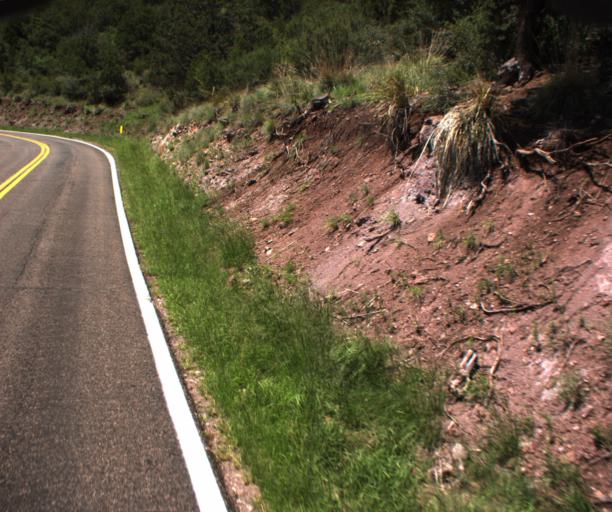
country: US
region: Arizona
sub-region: Greenlee County
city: Morenci
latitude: 33.2350
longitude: -109.3842
